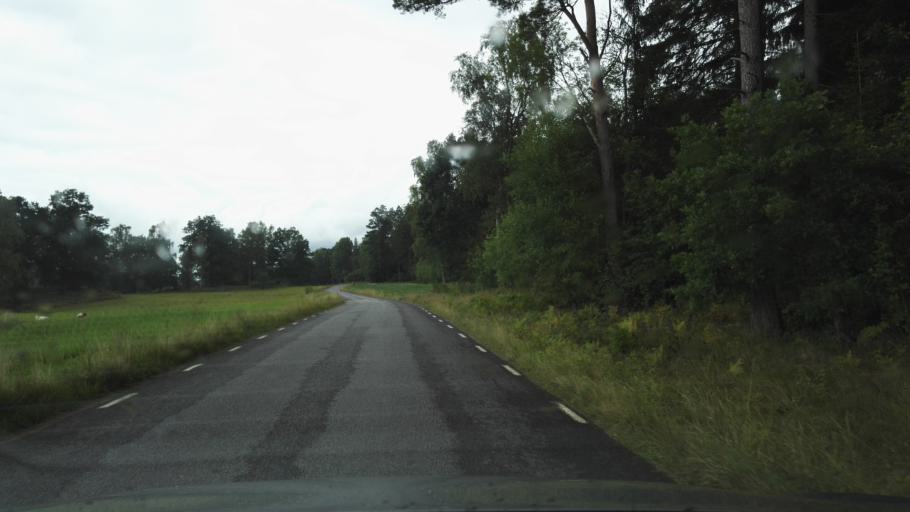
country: SE
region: Kronoberg
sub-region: Vaxjo Kommun
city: Rottne
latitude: 57.1051
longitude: 14.8020
